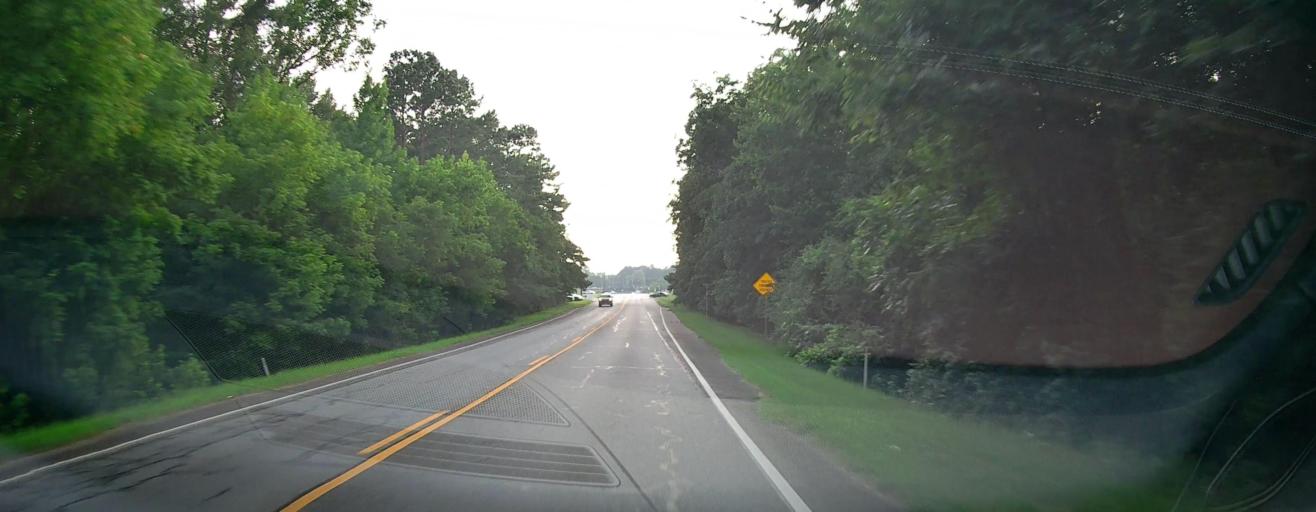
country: US
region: Georgia
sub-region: Jones County
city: Gray
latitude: 33.0150
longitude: -83.5200
